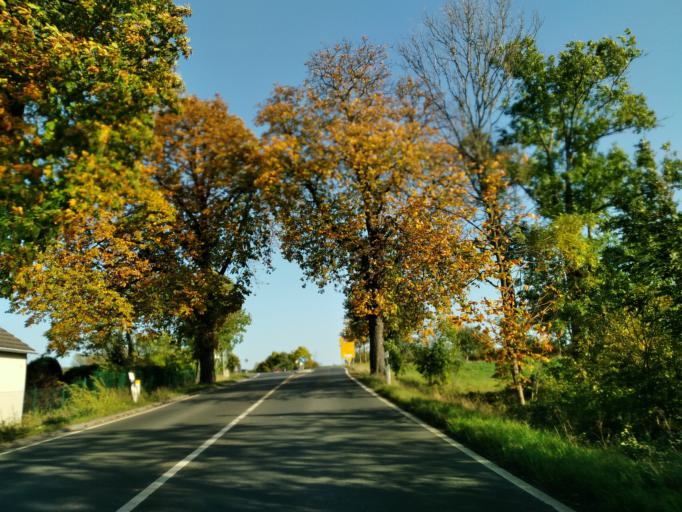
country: DE
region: Rheinland-Pfalz
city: Asbach
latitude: 50.7164
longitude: 7.3993
